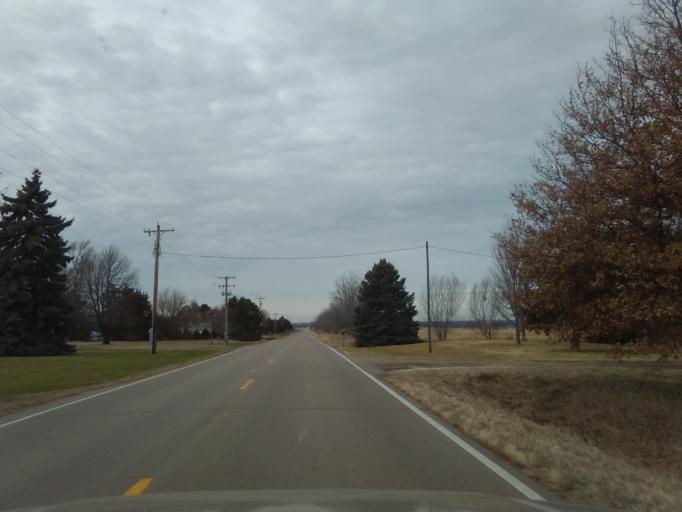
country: US
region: Nebraska
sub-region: Hall County
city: Grand Island
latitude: 40.7710
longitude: -98.3878
